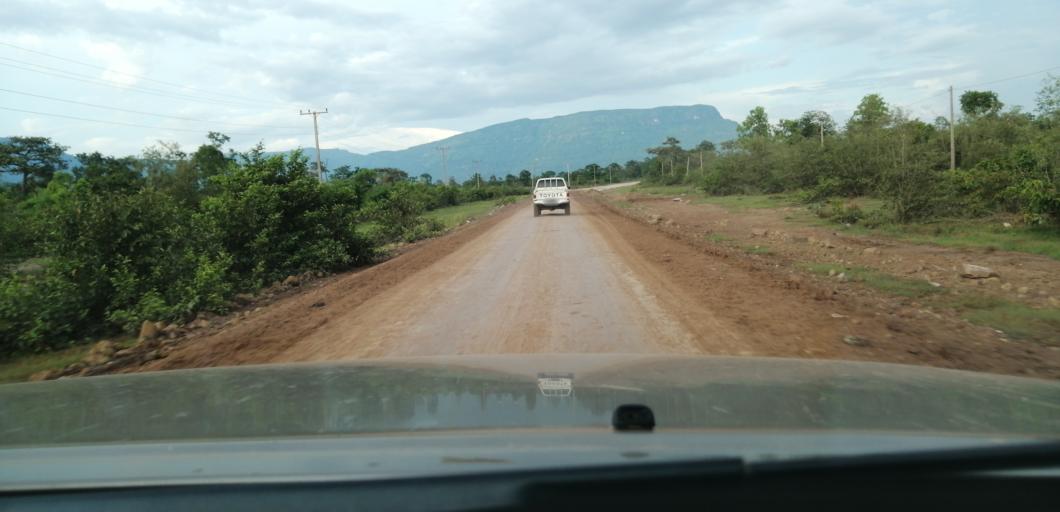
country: LA
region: Attapu
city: Attapu
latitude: 14.7098
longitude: 106.4853
